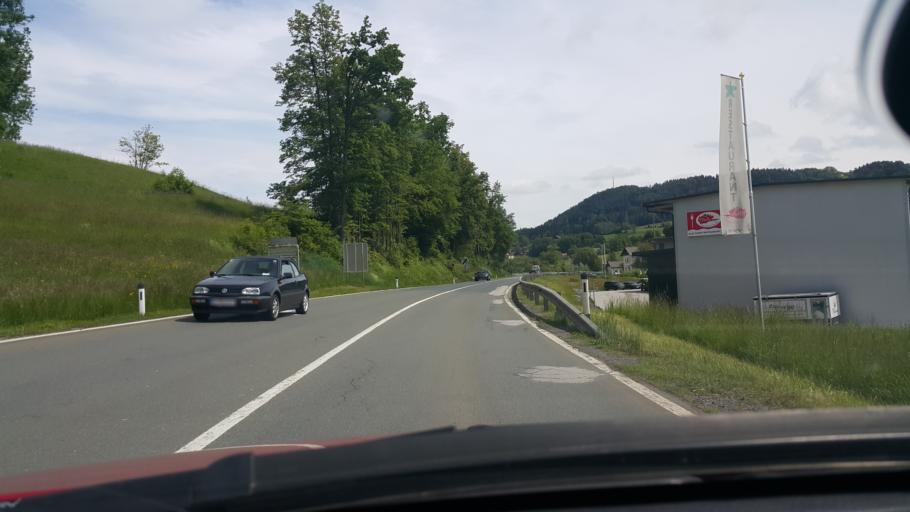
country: AT
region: Carinthia
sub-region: Politischer Bezirk Klagenfurt Land
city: Maria Rain
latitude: 46.5613
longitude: 14.2821
